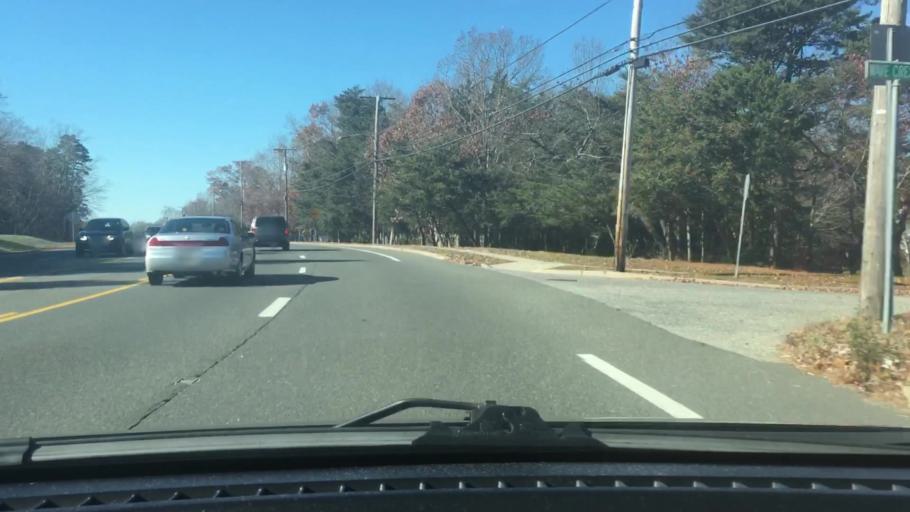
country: US
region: New Jersey
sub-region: Ocean County
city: Silver Ridge
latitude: 39.9916
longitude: -74.2044
